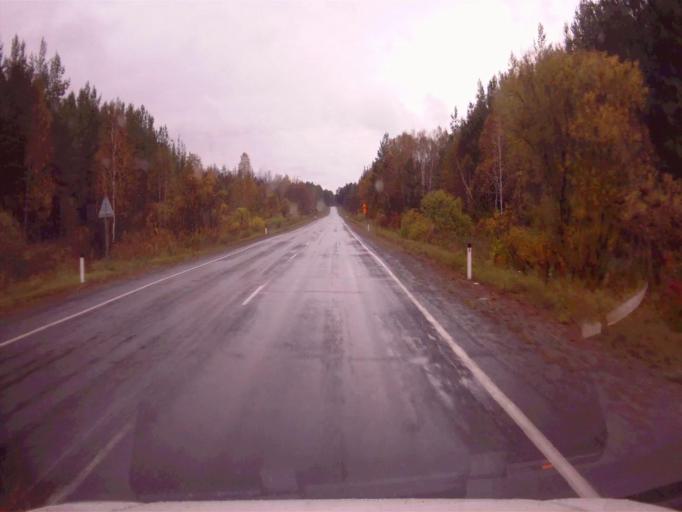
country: RU
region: Chelyabinsk
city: Verkhniy Ufaley
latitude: 56.0163
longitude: 60.3091
